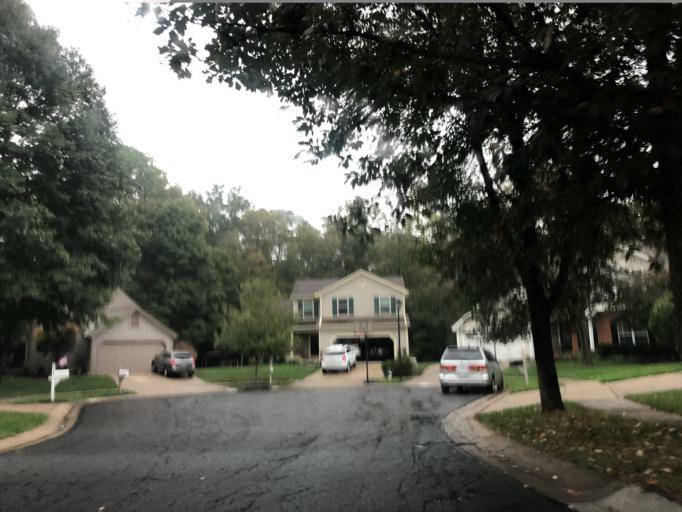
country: US
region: Ohio
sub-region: Hamilton County
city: Loveland
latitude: 39.2676
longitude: -84.2809
